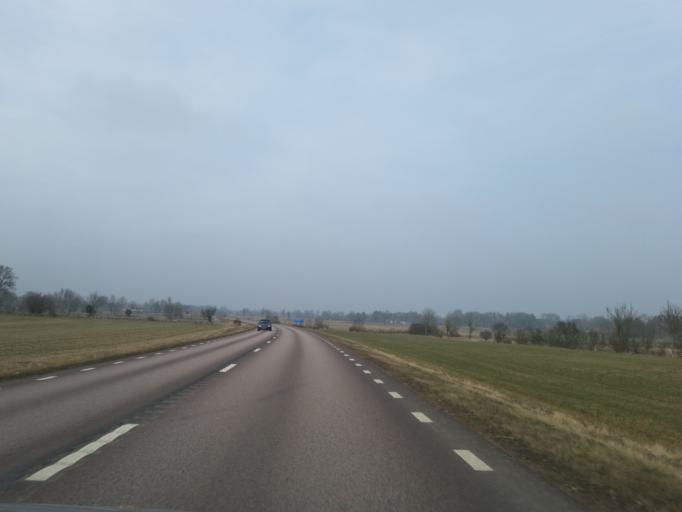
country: SE
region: Kalmar
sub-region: Borgholms Kommun
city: Borgholm
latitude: 57.1226
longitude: 16.9663
